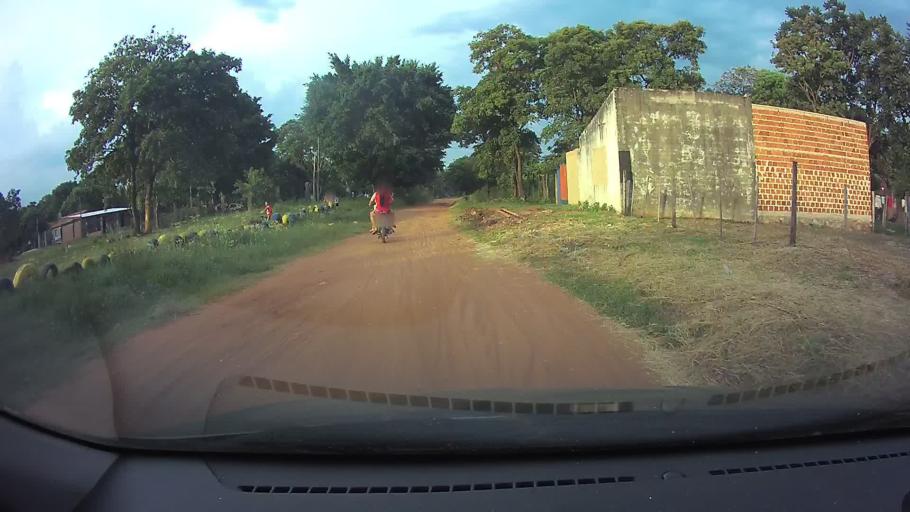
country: PY
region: Central
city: Limpio
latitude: -25.2445
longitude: -57.4498
